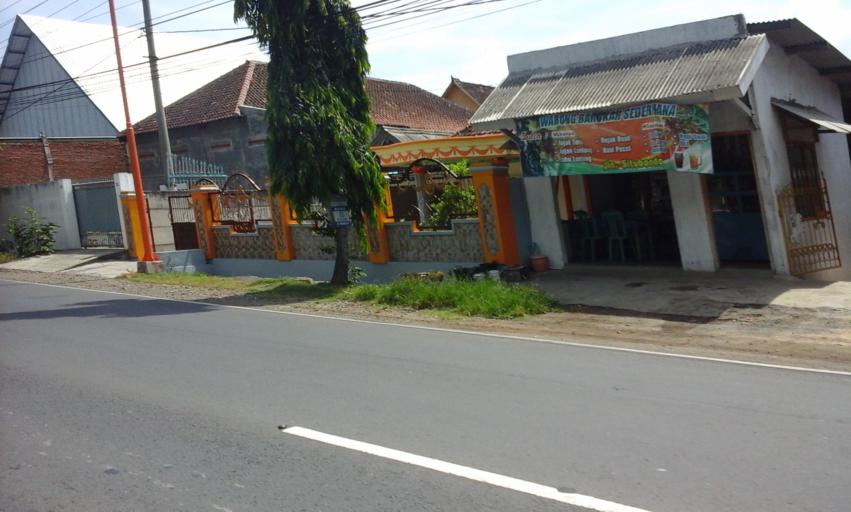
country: ID
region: East Java
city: Klatakan
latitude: -8.1218
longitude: 114.3978
